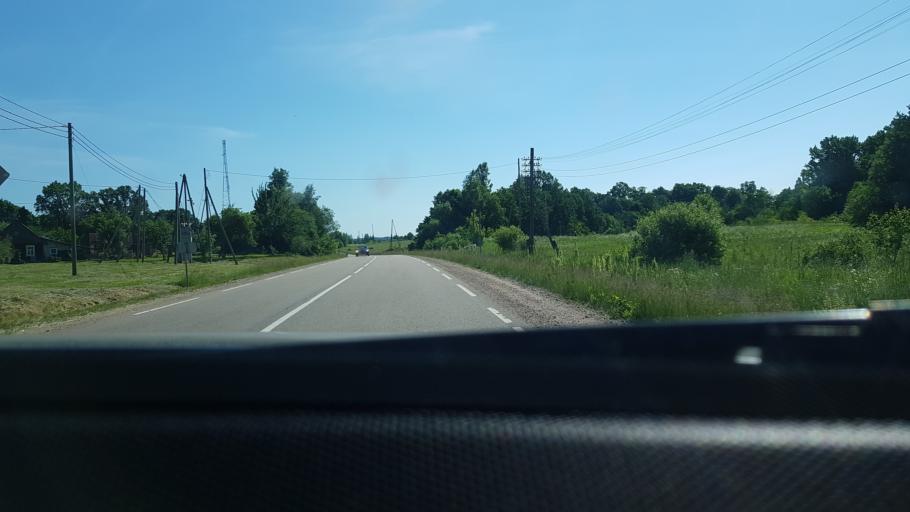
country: BY
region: Vitebsk
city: Braslaw
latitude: 55.8216
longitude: 26.8715
